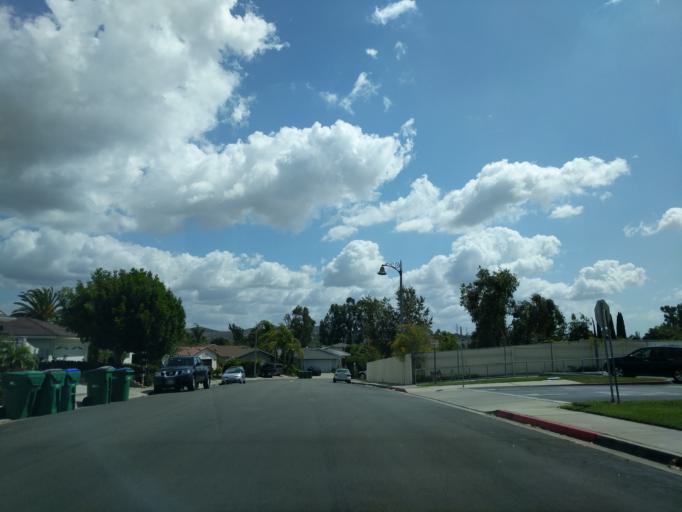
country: US
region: California
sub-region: Orange County
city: Ladera Ranch
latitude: 33.5701
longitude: -117.6540
